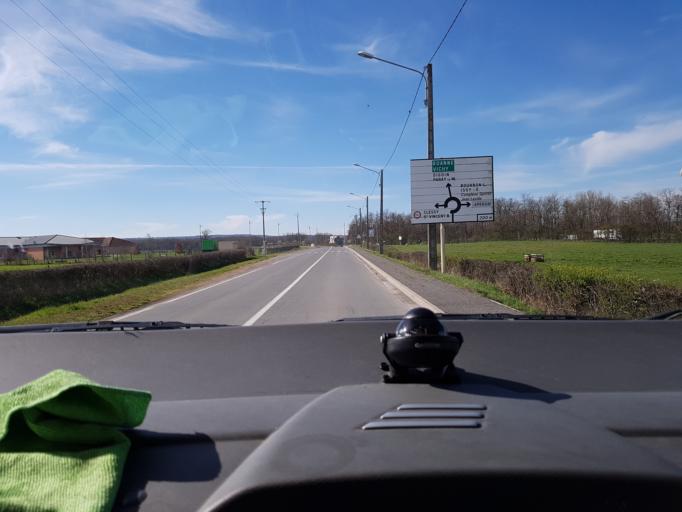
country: FR
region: Bourgogne
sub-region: Departement de Saone-et-Loire
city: Gueugnon
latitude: 46.5870
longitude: 4.0639
